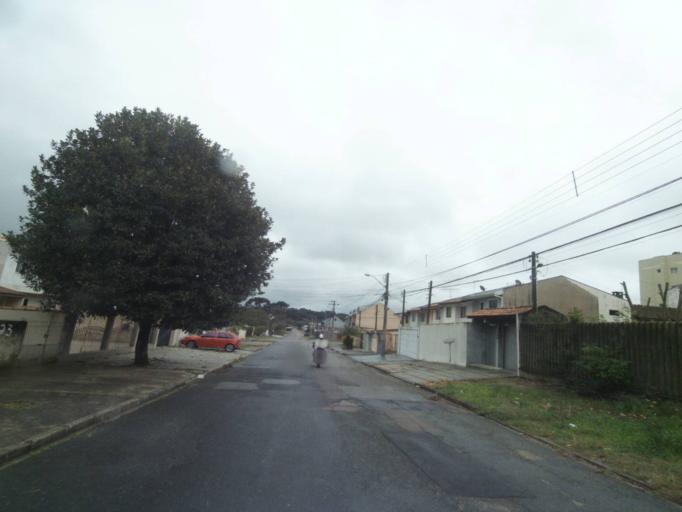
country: BR
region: Parana
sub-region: Curitiba
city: Curitiba
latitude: -25.5129
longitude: -49.3056
